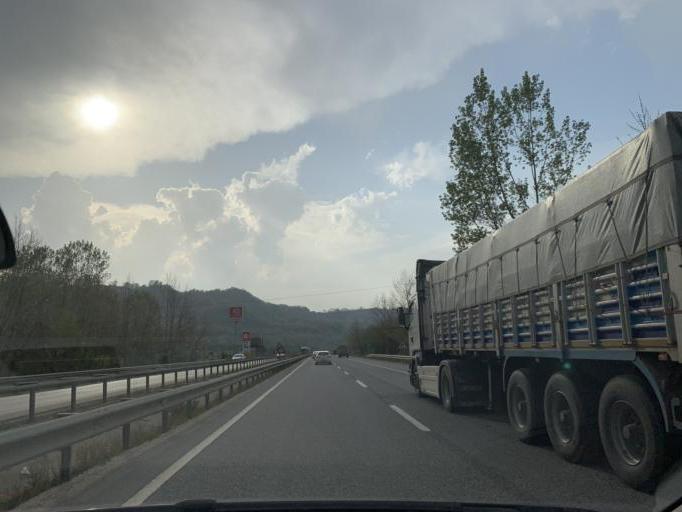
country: TR
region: Bursa
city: Tahtakopru
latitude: 39.9559
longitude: 29.6658
